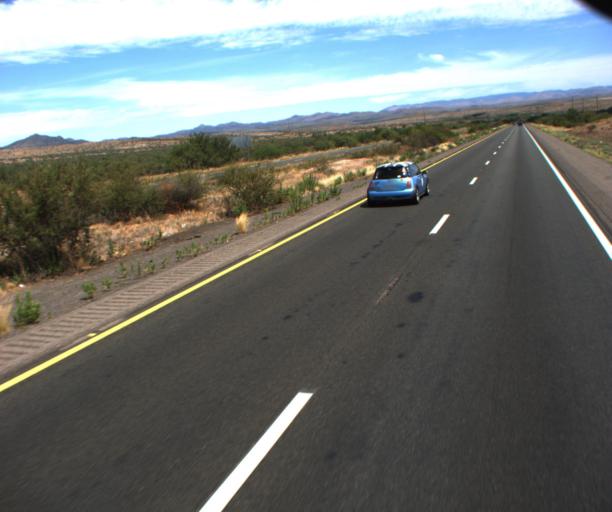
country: US
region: Arizona
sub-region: Yavapai County
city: Spring Valley
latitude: 34.3522
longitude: -112.1172
